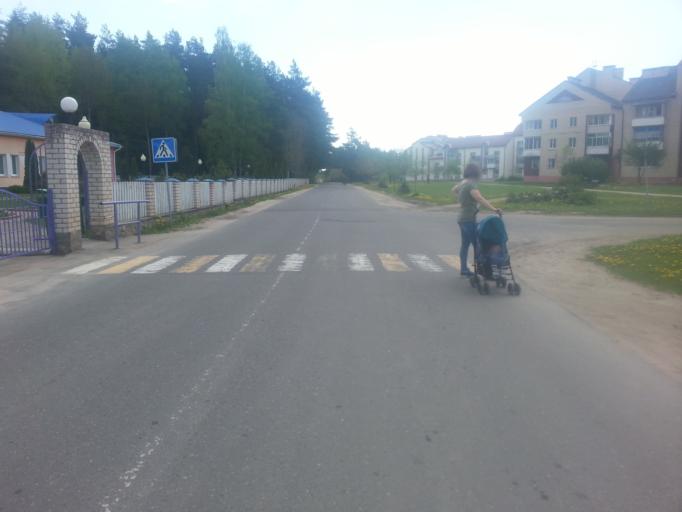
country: BY
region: Minsk
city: Narach
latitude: 54.9170
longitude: 26.7007
